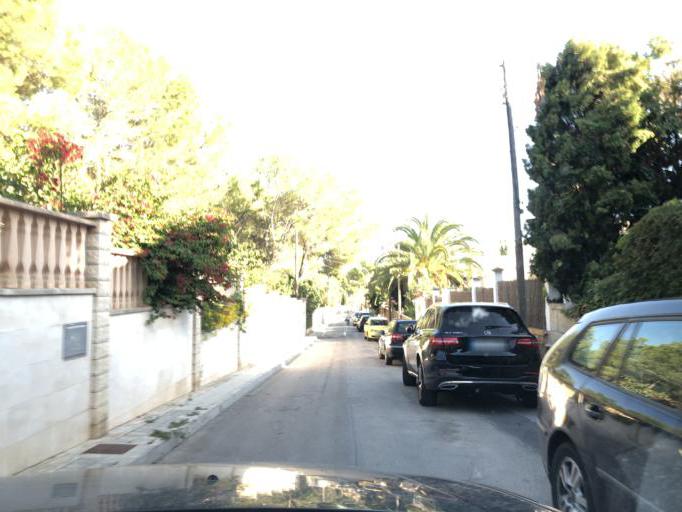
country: ES
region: Balearic Islands
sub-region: Illes Balears
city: Camp de Mar
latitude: 39.5402
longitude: 2.4398
